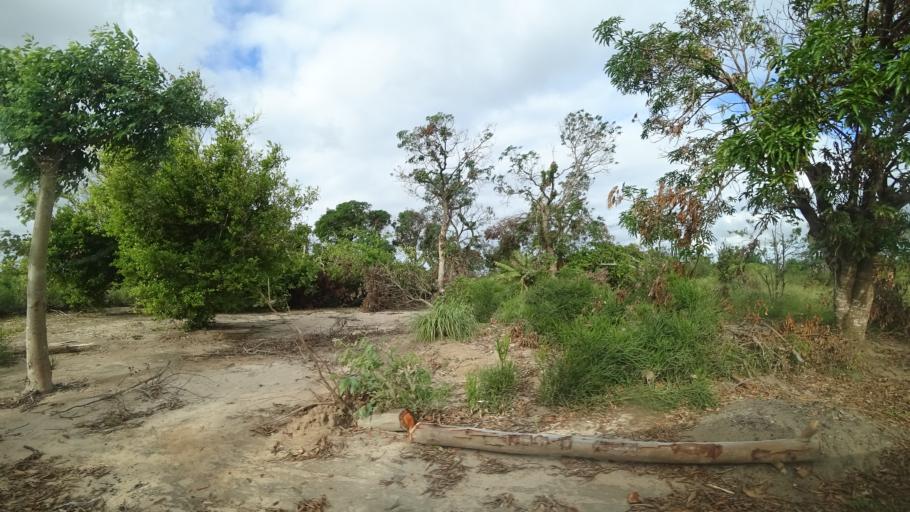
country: MZ
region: Sofala
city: Beira
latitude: -19.6353
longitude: 35.0595
